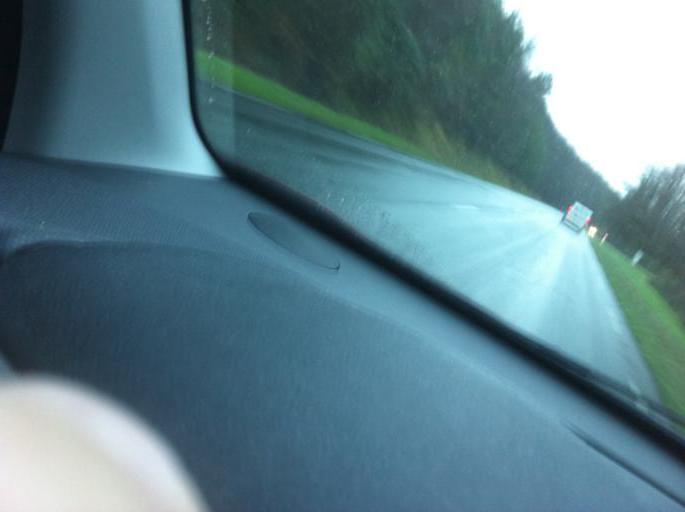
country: FR
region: Aquitaine
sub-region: Departement de la Dordogne
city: Chancelade
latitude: 45.1945
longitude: 0.6205
